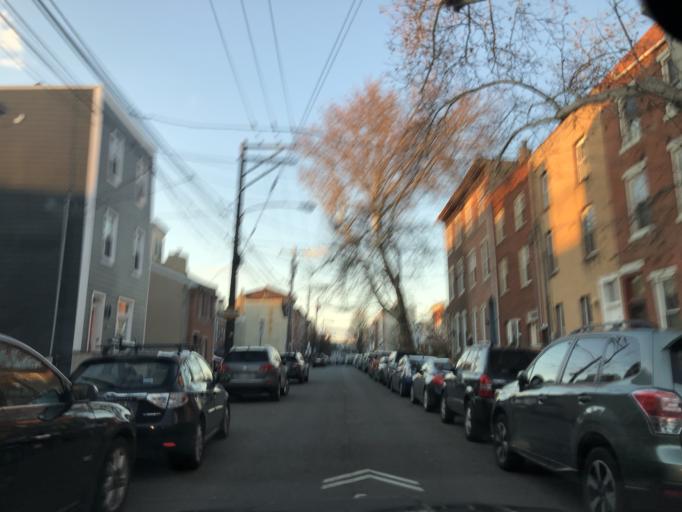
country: US
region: Pennsylvania
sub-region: Philadelphia County
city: Philadelphia
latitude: 39.9712
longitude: -75.1325
